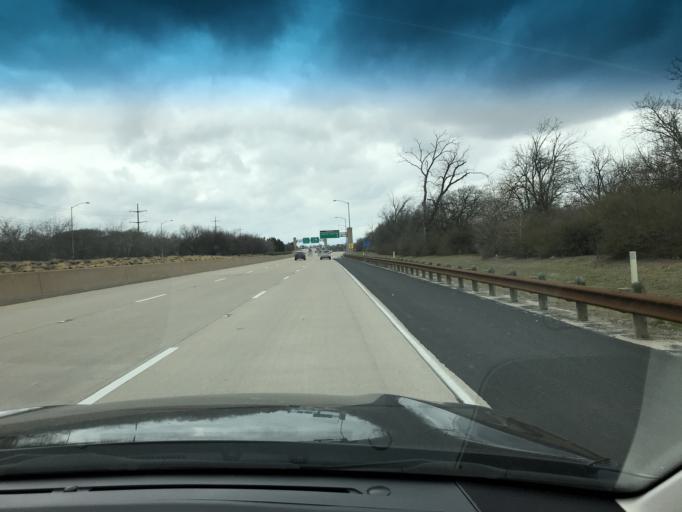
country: US
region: Texas
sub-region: Tarrant County
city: Westworth
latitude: 32.7153
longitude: -97.3926
